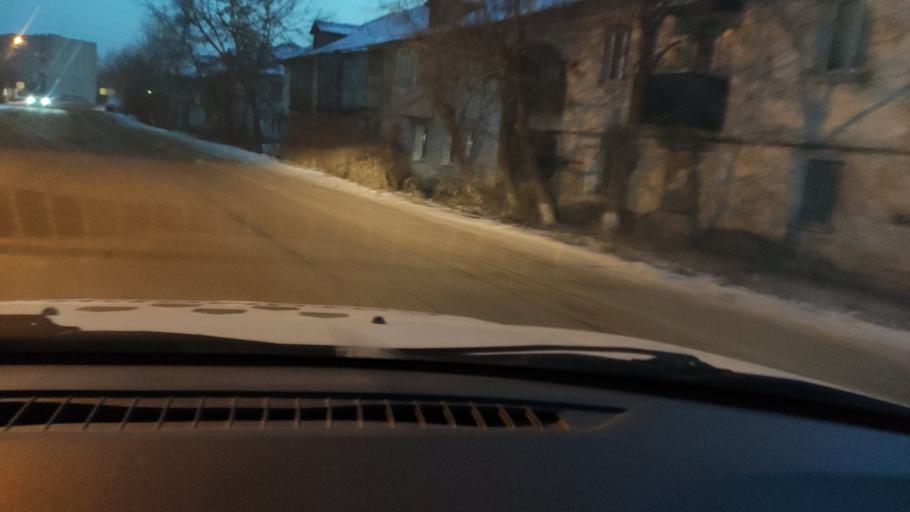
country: RU
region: Perm
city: Kungur
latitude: 57.4355
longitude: 56.9304
